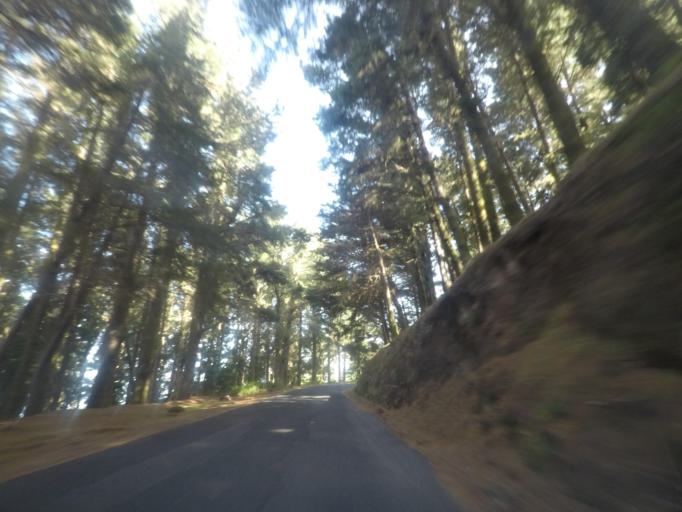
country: PT
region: Madeira
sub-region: Santa Cruz
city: Camacha
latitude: 32.7048
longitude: -16.8792
